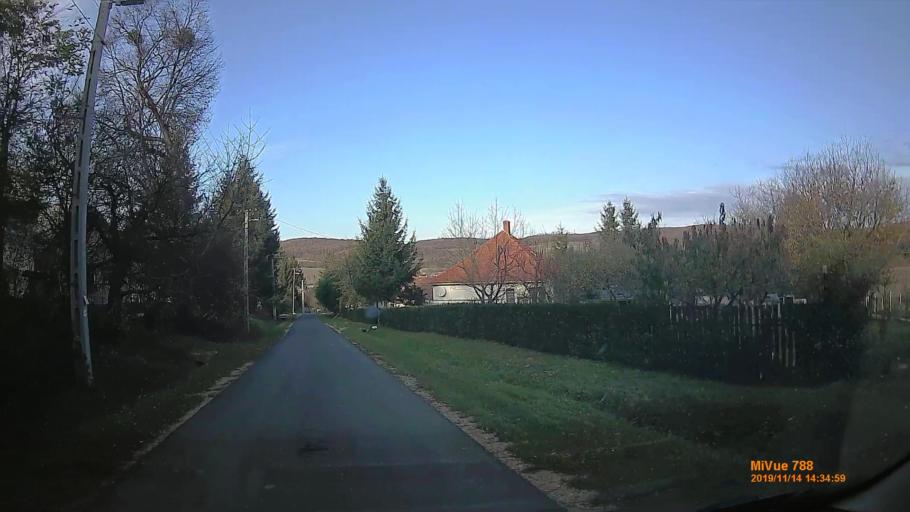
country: HU
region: Veszprem
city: Zirc
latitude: 47.2228
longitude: 17.7901
